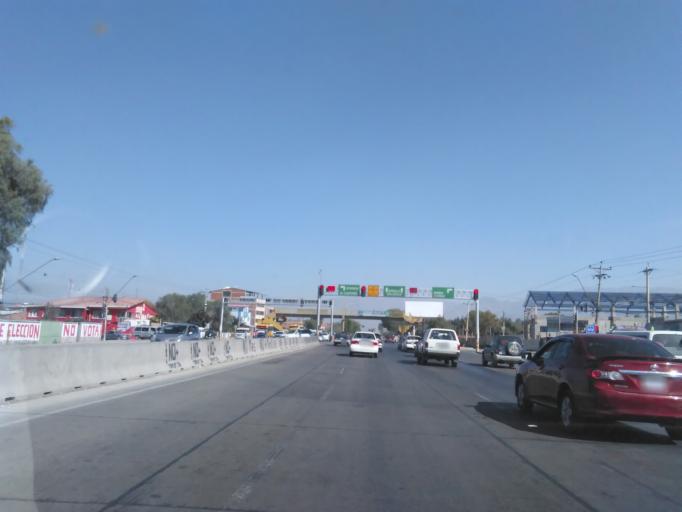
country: BO
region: Cochabamba
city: Cochabamba
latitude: -17.3919
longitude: -66.2589
